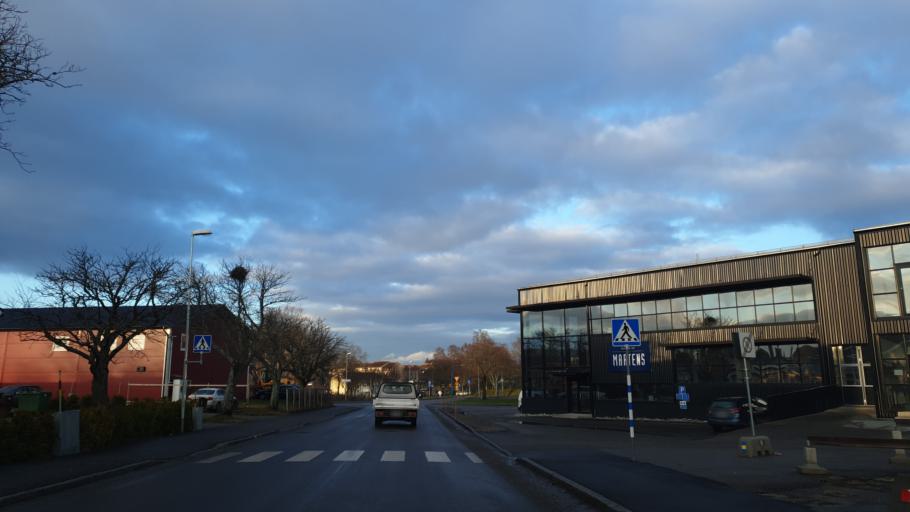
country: SE
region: Gaevleborg
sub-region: Hudiksvalls Kommun
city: Hudiksvall
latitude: 61.7247
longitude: 17.1263
